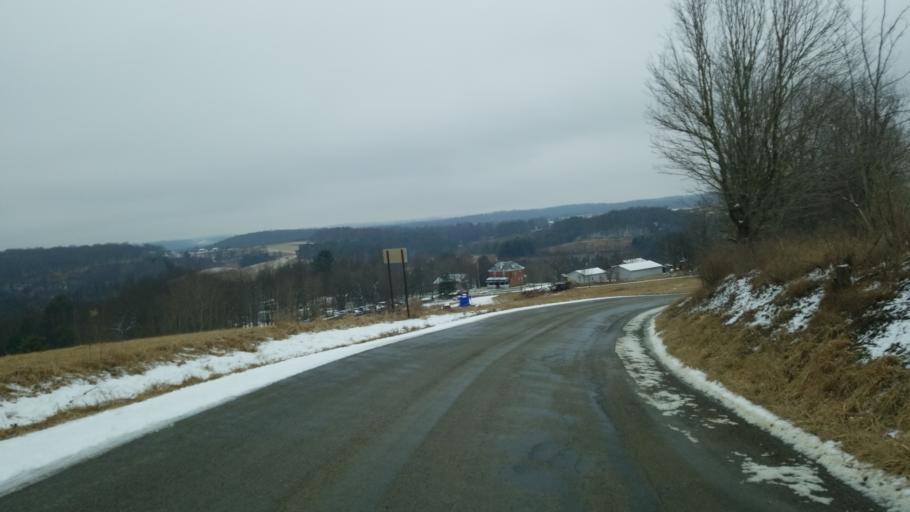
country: US
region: Pennsylvania
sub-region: Jefferson County
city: Reynoldsville
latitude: 41.0865
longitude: -78.8527
